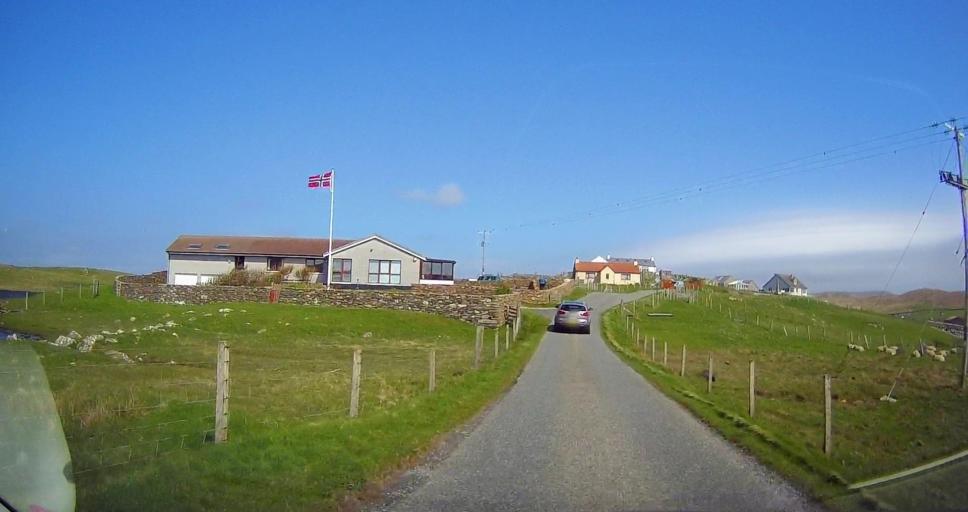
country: GB
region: Scotland
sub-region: Shetland Islands
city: Sandwick
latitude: 60.0816
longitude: -1.3349
